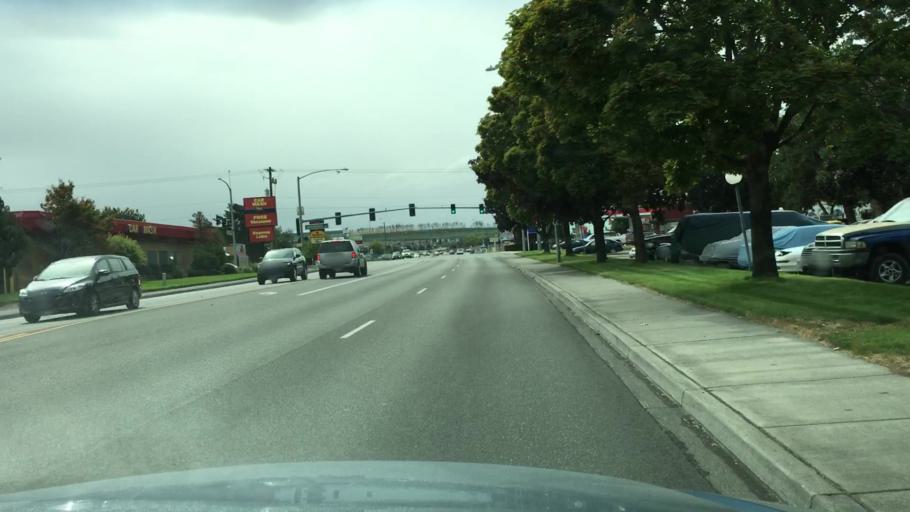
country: US
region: Washington
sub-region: Franklin County
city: West Pasco
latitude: 46.2136
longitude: -119.2256
